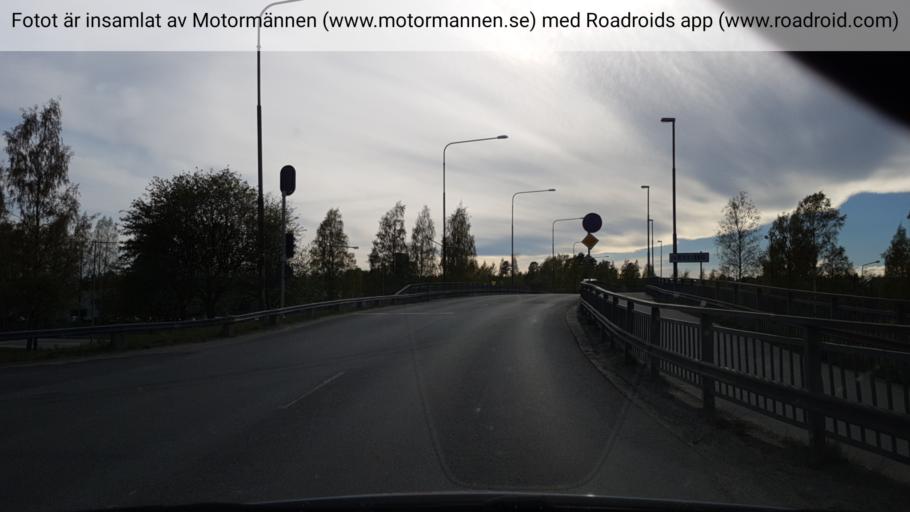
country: SE
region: Vaesterbotten
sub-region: Umea Kommun
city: Umea
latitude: 63.8154
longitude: 20.2514
